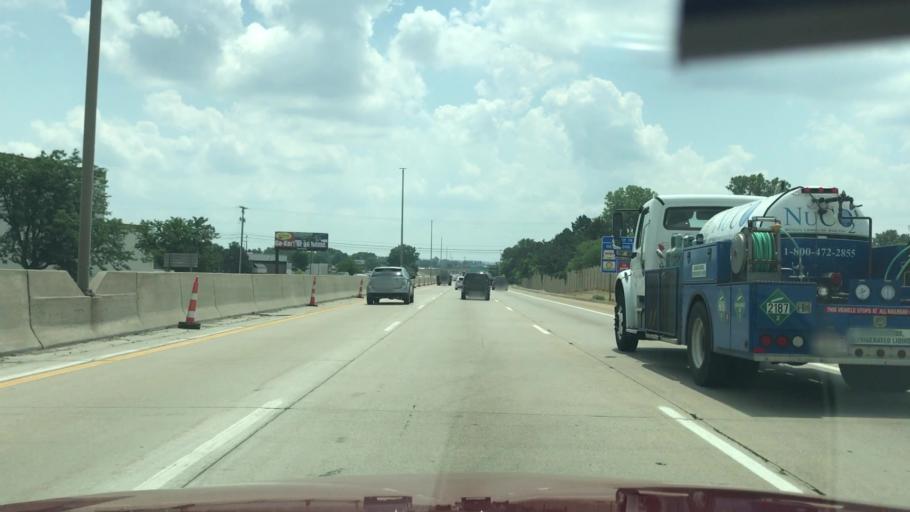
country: US
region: Michigan
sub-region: Kent County
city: Kentwood
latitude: 42.8747
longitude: -85.6817
